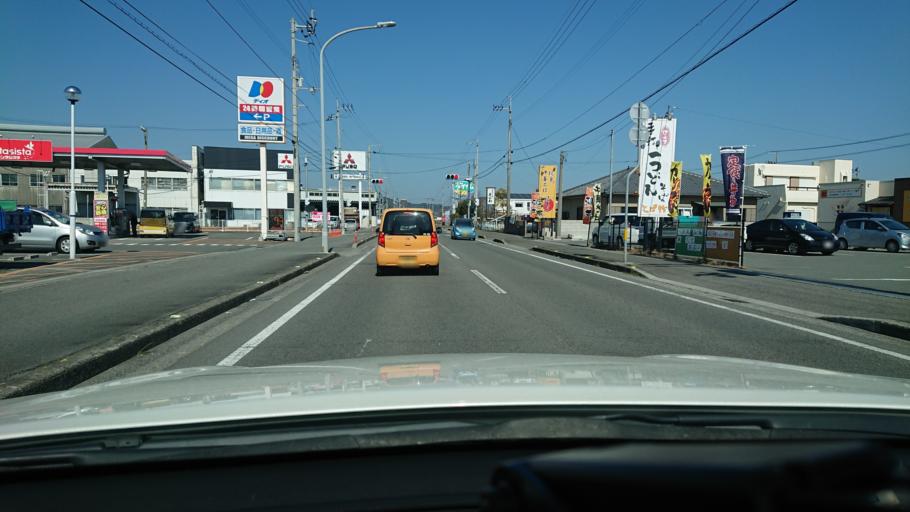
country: JP
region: Tokushima
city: Narutocho-mitsuishi
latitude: 34.1462
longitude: 134.5935
